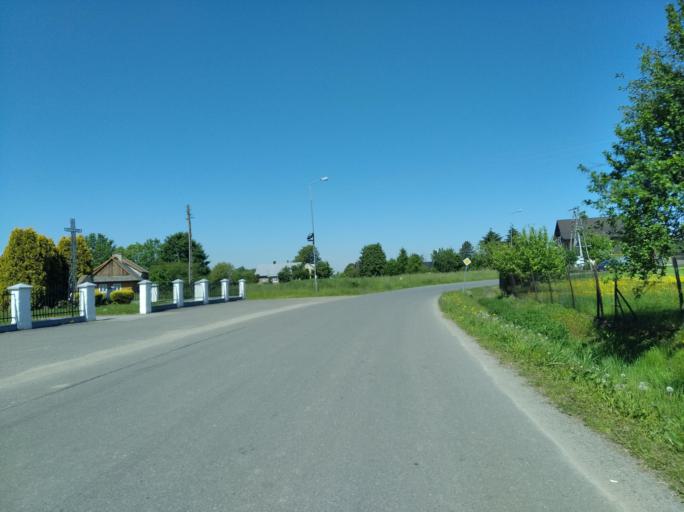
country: PL
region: Subcarpathian Voivodeship
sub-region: Krosno
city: Krosno
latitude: 49.7205
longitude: 21.7713
